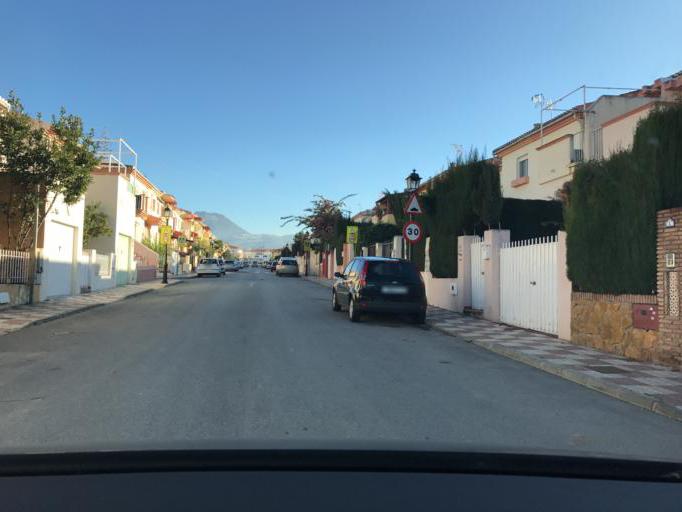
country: ES
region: Andalusia
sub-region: Provincia de Granada
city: Pulianas
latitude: 37.2160
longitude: -3.6055
